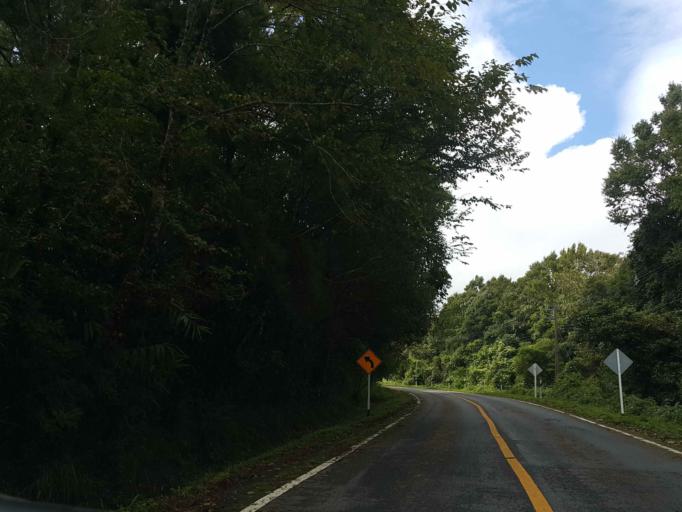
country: TH
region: Chiang Mai
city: Mae Chaem
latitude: 18.5410
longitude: 98.4886
